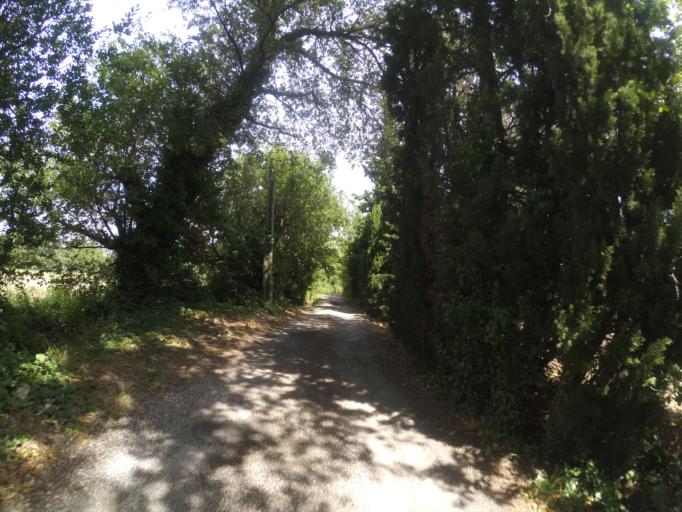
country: FR
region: Languedoc-Roussillon
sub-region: Departement des Pyrenees-Orientales
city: Ille-sur-Tet
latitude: 42.6805
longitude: 2.6424
